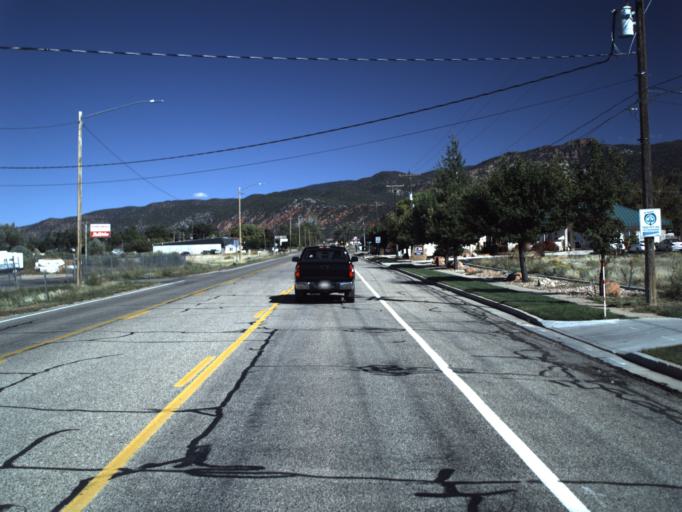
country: US
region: Utah
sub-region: Iron County
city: Parowan
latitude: 37.8386
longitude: -112.8454
